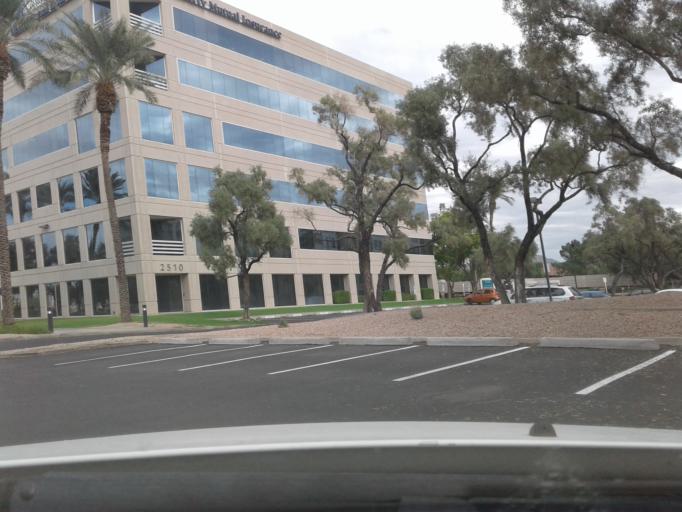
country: US
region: Arizona
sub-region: Maricopa County
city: Glendale
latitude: 33.5688
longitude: -112.1142
